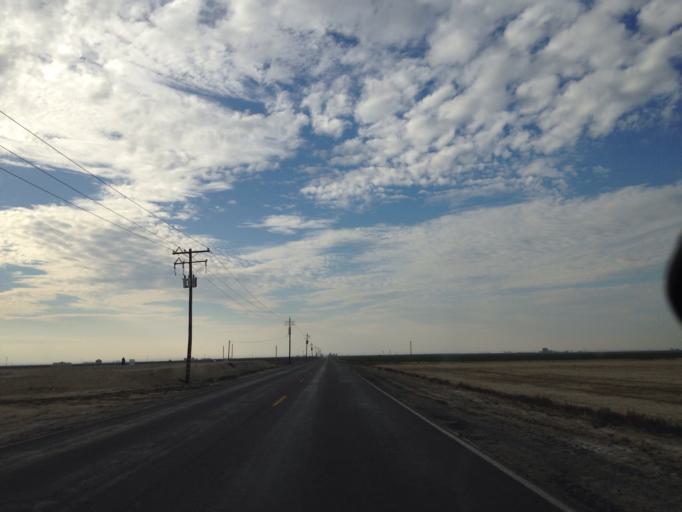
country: US
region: California
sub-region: Kern County
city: Buttonwillow
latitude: 35.4424
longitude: -119.4906
